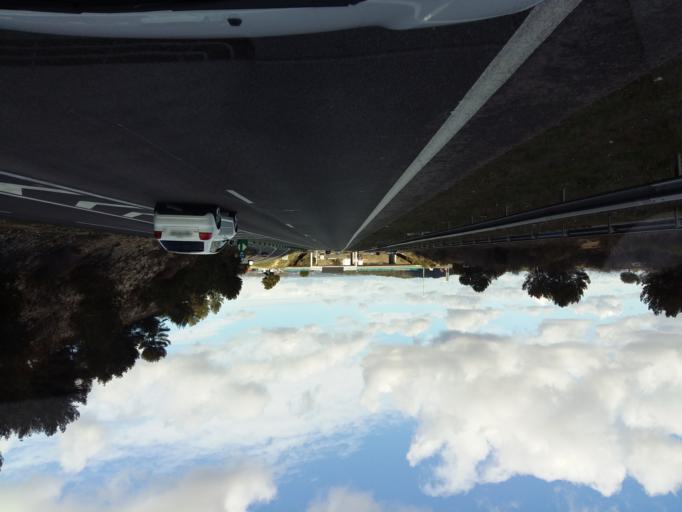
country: FR
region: Provence-Alpes-Cote d'Azur
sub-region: Departement des Bouches-du-Rhone
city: Bouc-Bel-Air
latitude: 43.4691
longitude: 5.4073
